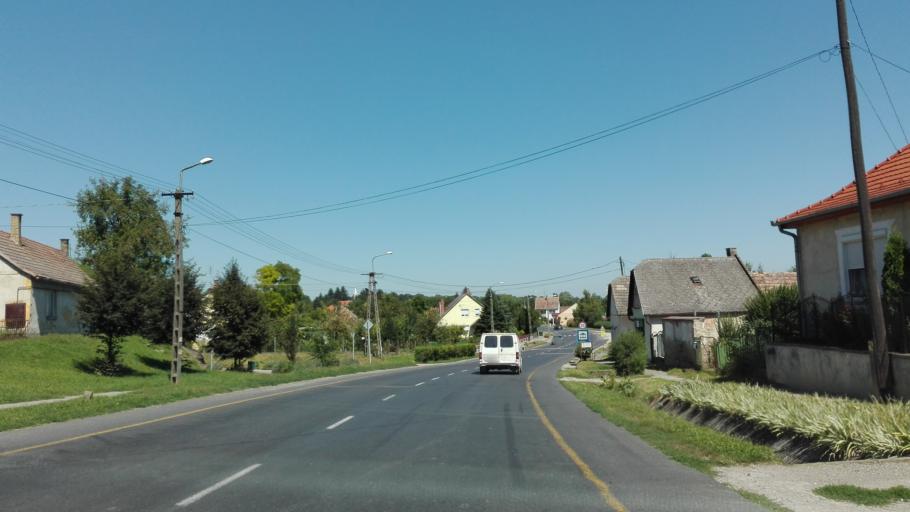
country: HU
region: Fejer
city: Mezoszilas
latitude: 46.8131
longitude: 18.4814
